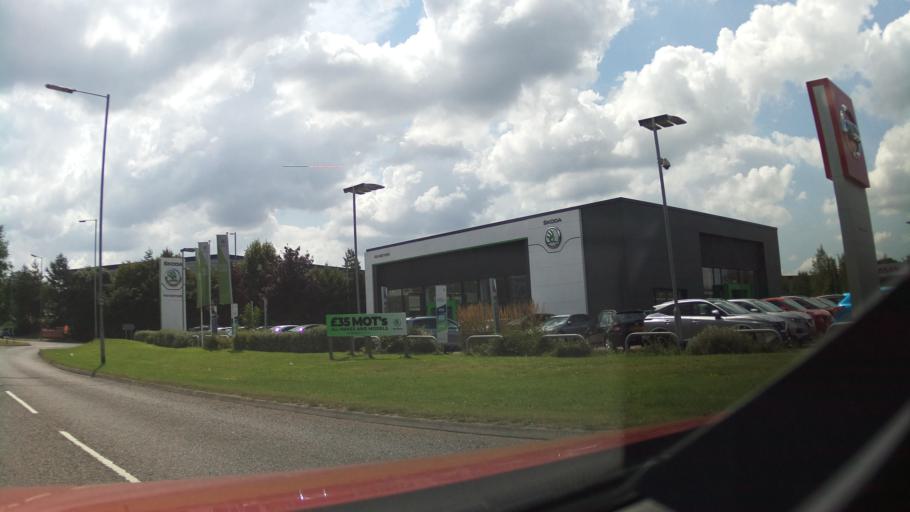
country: GB
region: England
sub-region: Wiltshire
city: Lydiard Tregoze
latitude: 51.5752
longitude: -1.8319
